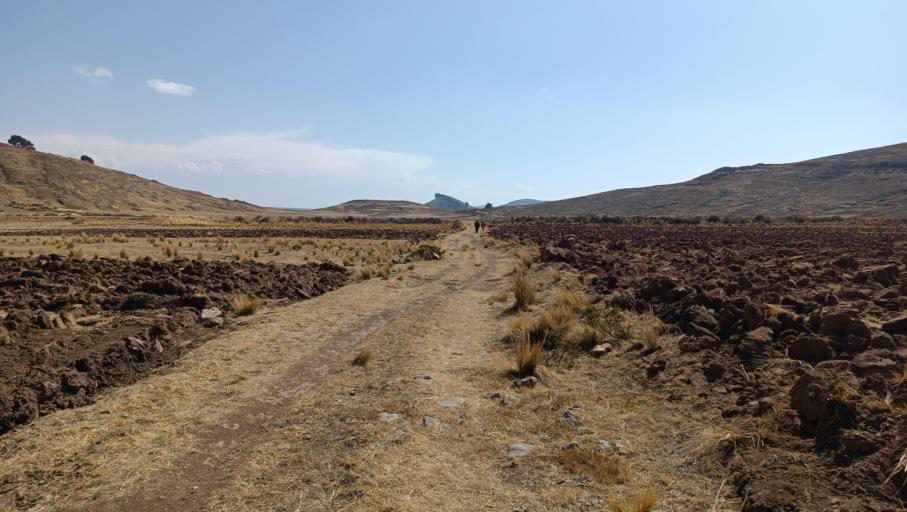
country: BO
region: La Paz
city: Batallas
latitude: -16.3484
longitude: -68.6645
